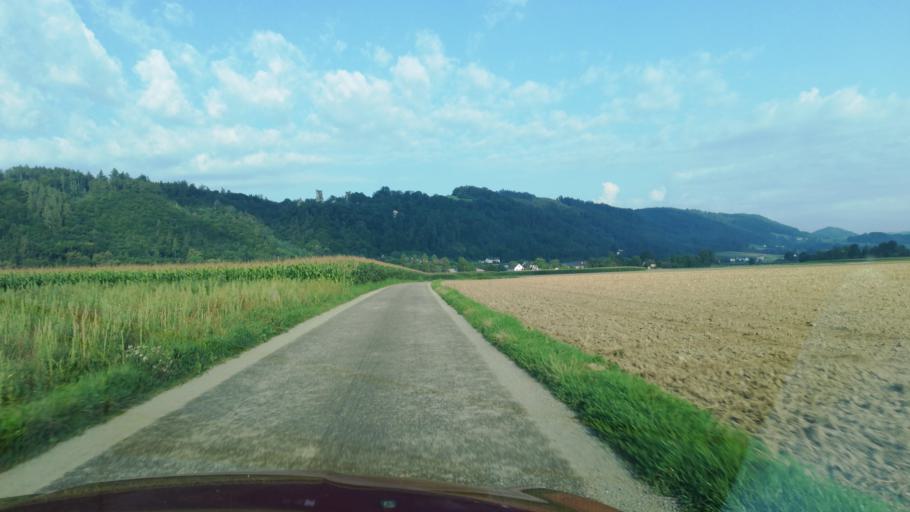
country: AT
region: Upper Austria
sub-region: Politischer Bezirk Urfahr-Umgebung
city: Feldkirchen an der Donau
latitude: 48.3397
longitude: 13.9938
